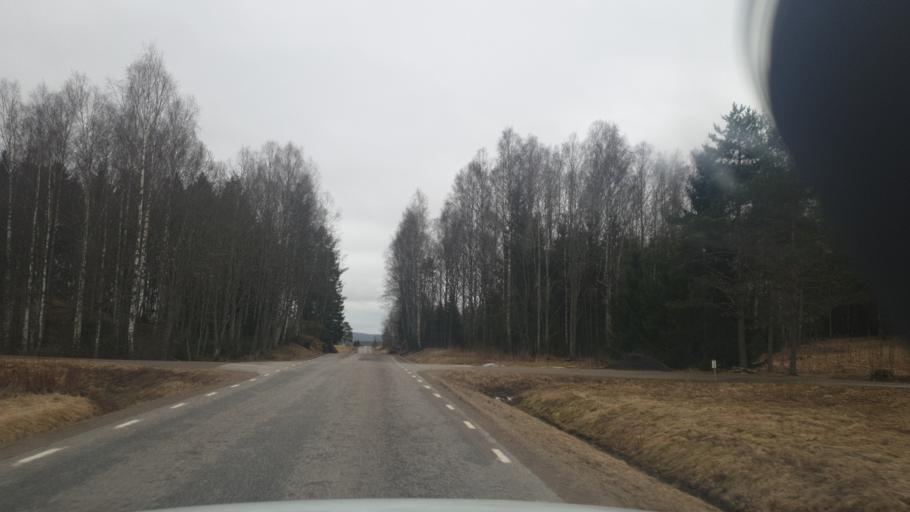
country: SE
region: Vaermland
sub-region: Eda Kommun
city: Charlottenberg
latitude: 59.7906
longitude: 12.1552
